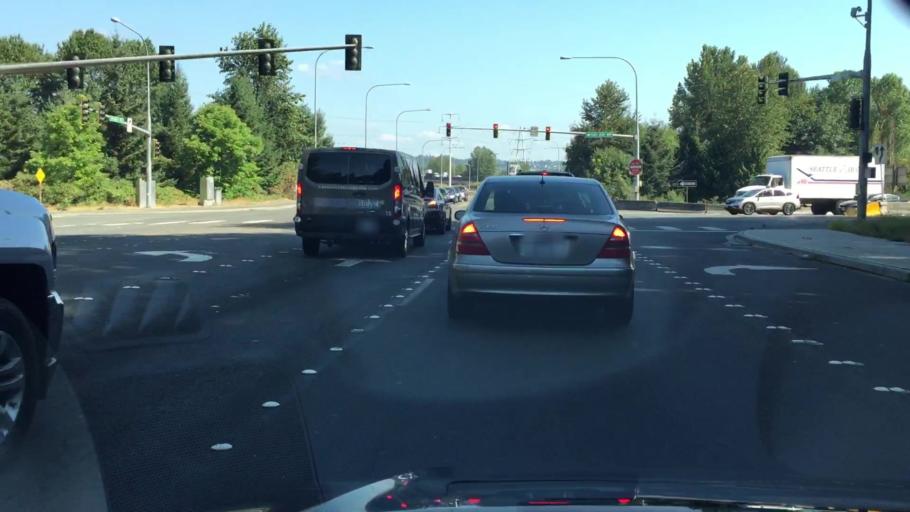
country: US
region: Washington
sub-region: King County
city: Tukwila
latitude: 47.4659
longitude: -122.2494
